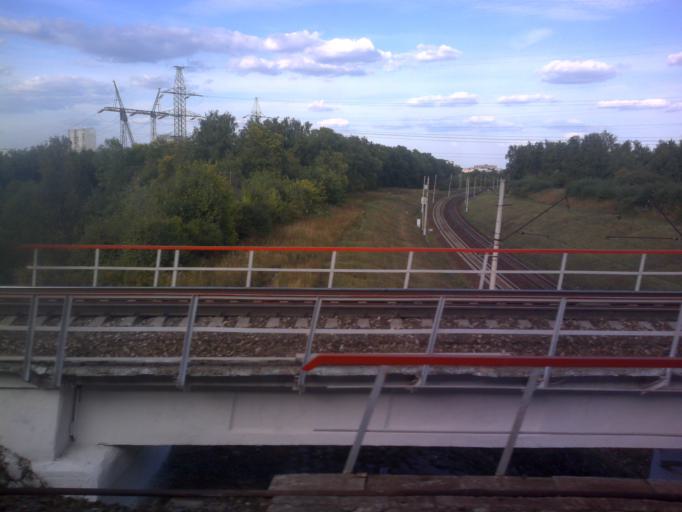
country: RU
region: Moscow
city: Tsaritsyno
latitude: 55.6107
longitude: 37.6405
